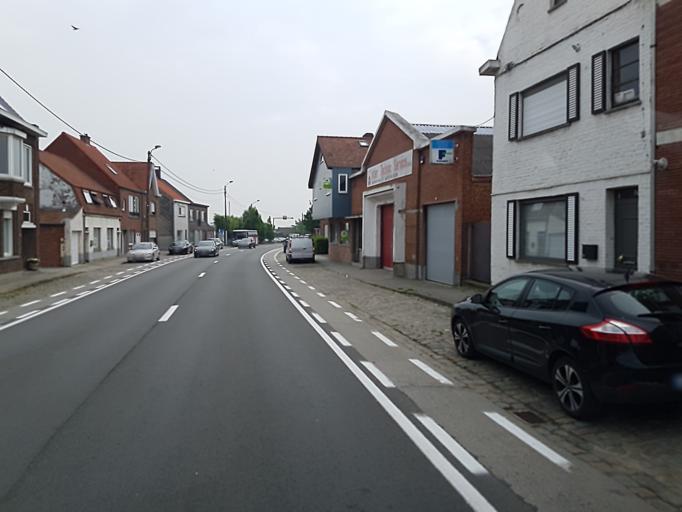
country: BE
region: Flanders
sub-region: Provincie West-Vlaanderen
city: Tielt
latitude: 50.9891
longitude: 3.3350
